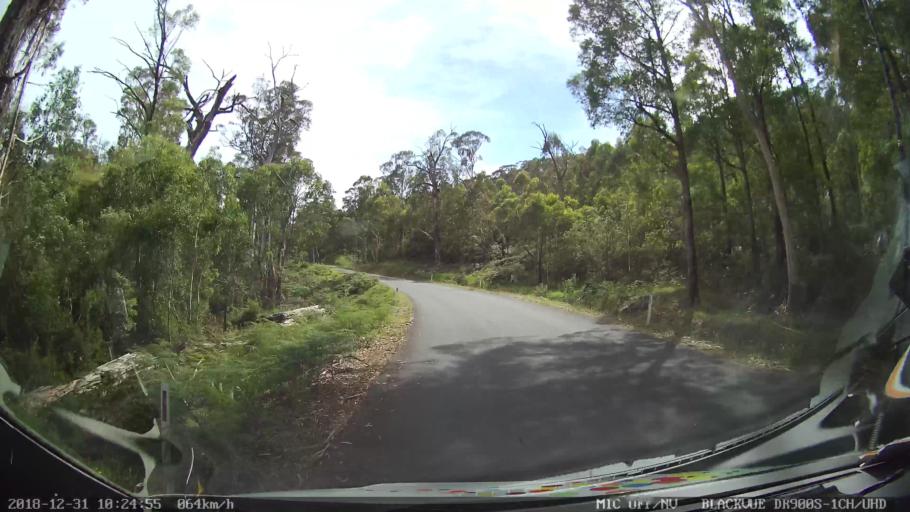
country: AU
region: New South Wales
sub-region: Snowy River
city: Jindabyne
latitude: -36.5106
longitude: 148.1449
